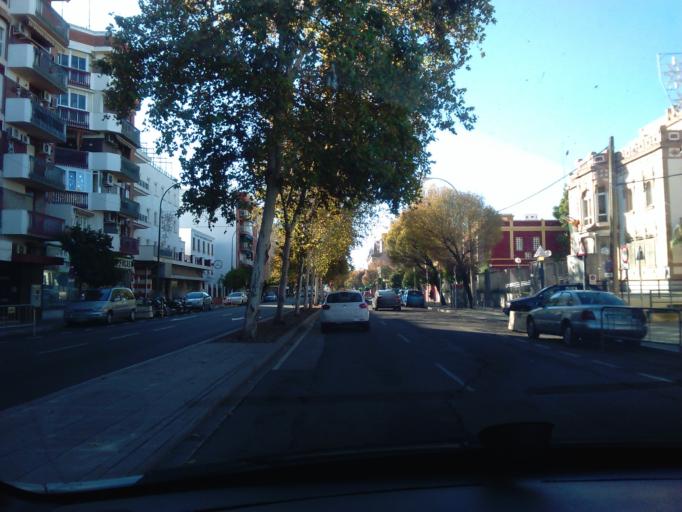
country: ES
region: Andalusia
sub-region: Provincia de Sevilla
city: Sevilla
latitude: 37.3856
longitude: -5.9653
